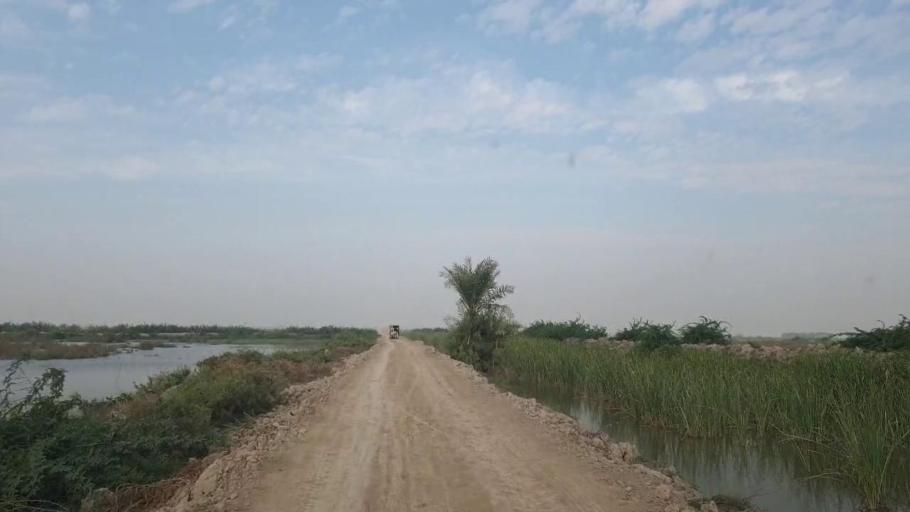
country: PK
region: Sindh
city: Tando Bago
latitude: 24.8652
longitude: 68.9894
